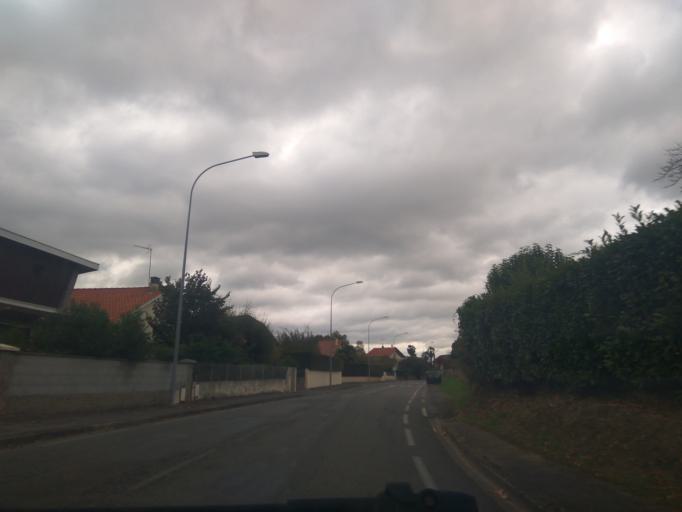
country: FR
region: Aquitaine
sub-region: Departement des Pyrenees-Atlantiques
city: Bizanos
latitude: 43.2892
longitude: -0.3431
